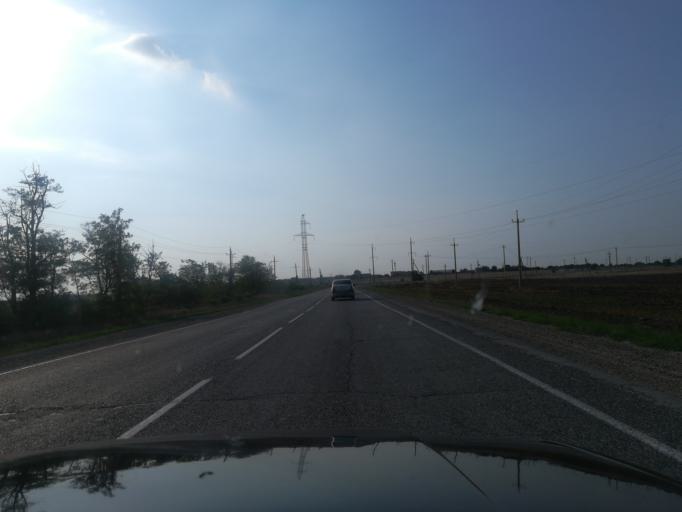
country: RU
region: Krasnodarskiy
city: Yurovka
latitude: 45.1034
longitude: 37.4239
